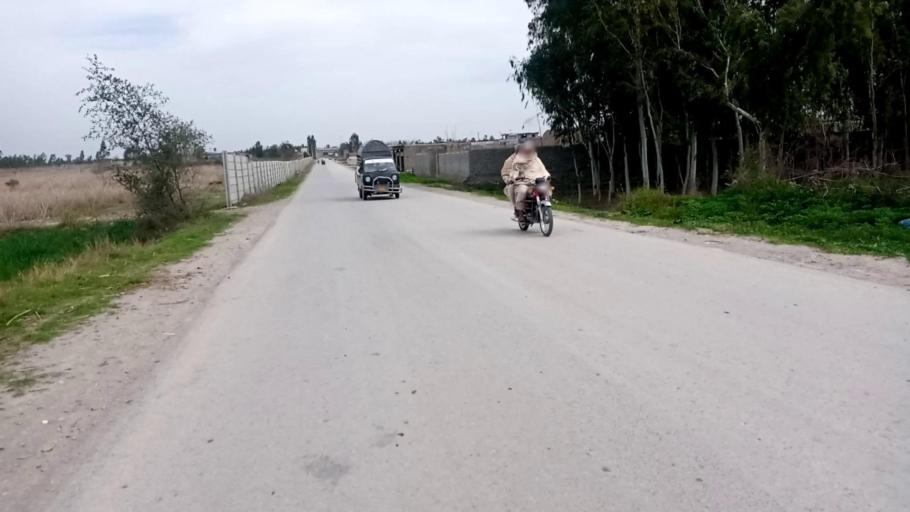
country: PK
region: Khyber Pakhtunkhwa
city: Charsadda
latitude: 34.0618
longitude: 71.6995
